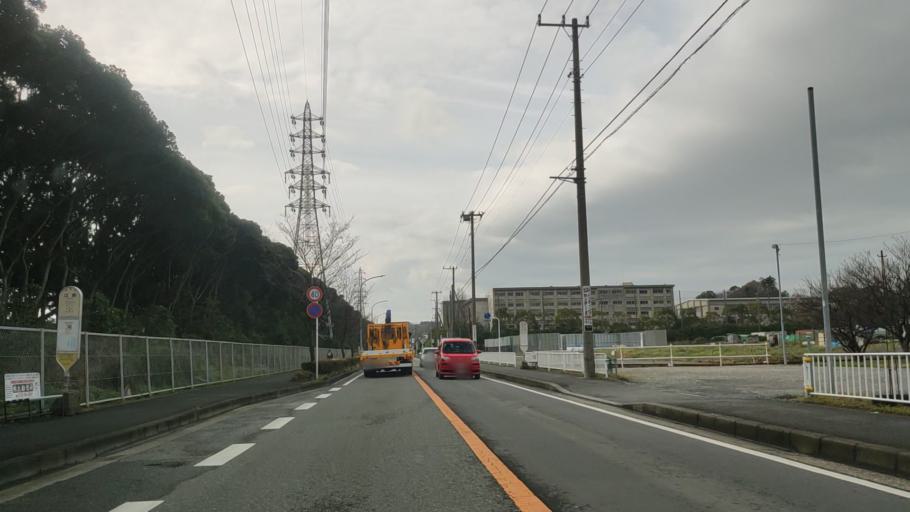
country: JP
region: Kanagawa
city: Fujisawa
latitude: 35.3765
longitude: 139.5252
